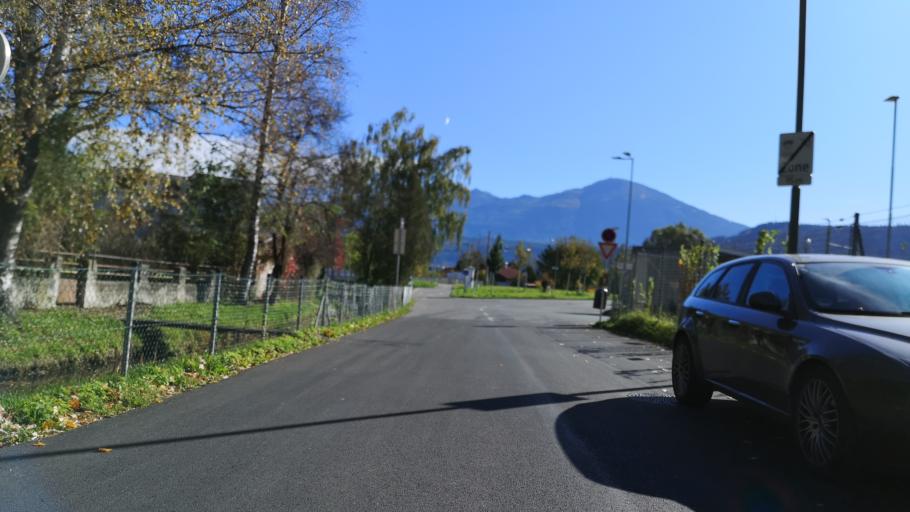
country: AT
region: Tyrol
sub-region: Politischer Bezirk Innsbruck Land
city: Vols
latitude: 47.2644
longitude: 11.3619
